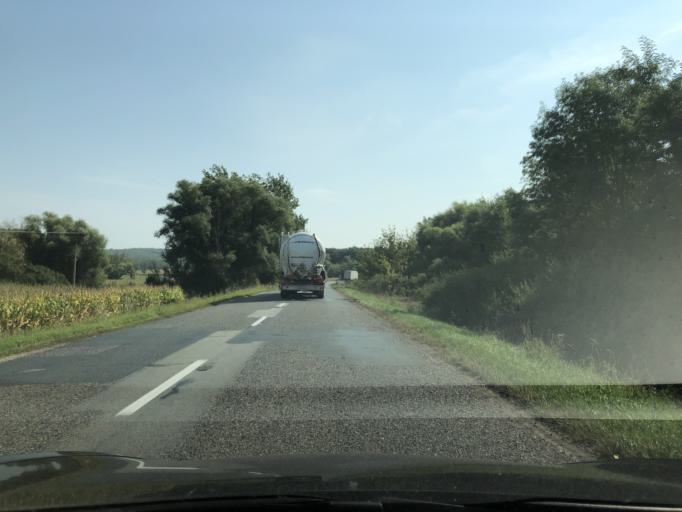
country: CZ
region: South Moravian
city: Drnholec
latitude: 48.8538
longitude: 16.4995
